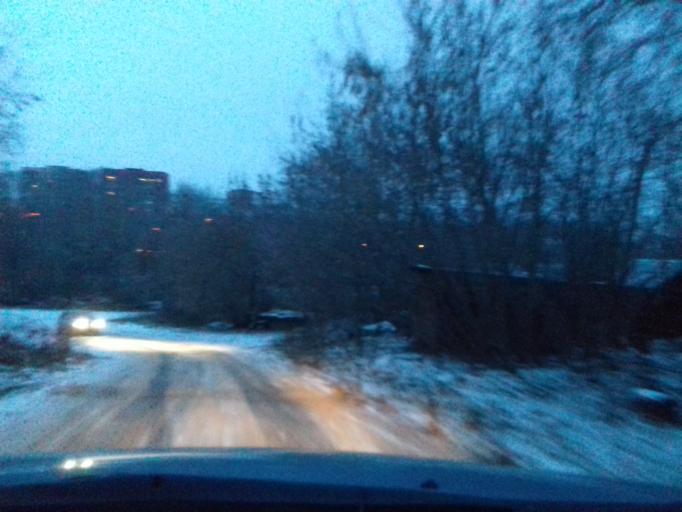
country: RU
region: Sverdlovsk
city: Istok
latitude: 56.7469
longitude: 60.6935
